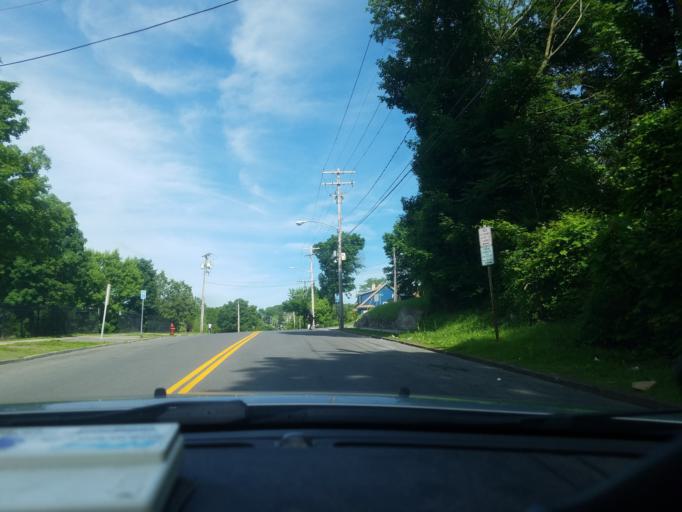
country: US
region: New York
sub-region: Onondaga County
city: Syracuse
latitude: 43.0482
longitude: -76.1178
